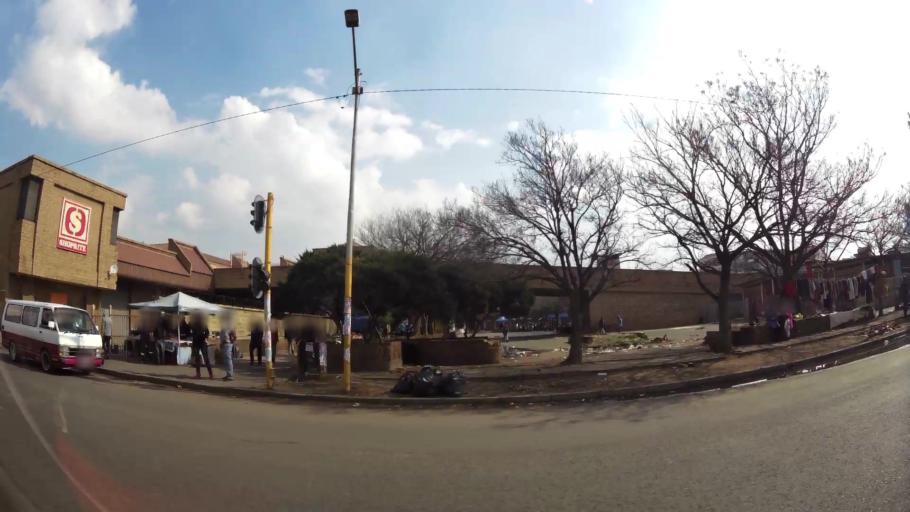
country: ZA
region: Gauteng
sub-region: Sedibeng District Municipality
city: Vereeniging
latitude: -26.6753
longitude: 27.9337
